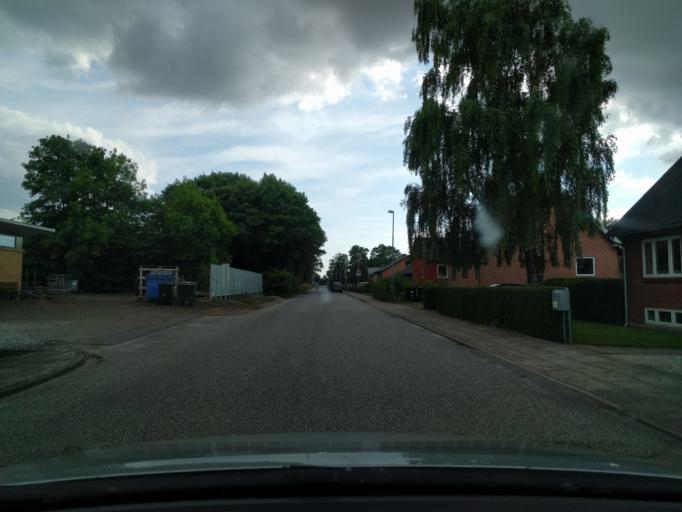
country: DK
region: Central Jutland
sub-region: Herning Kommune
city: Snejbjerg
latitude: 56.0915
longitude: 8.9098
